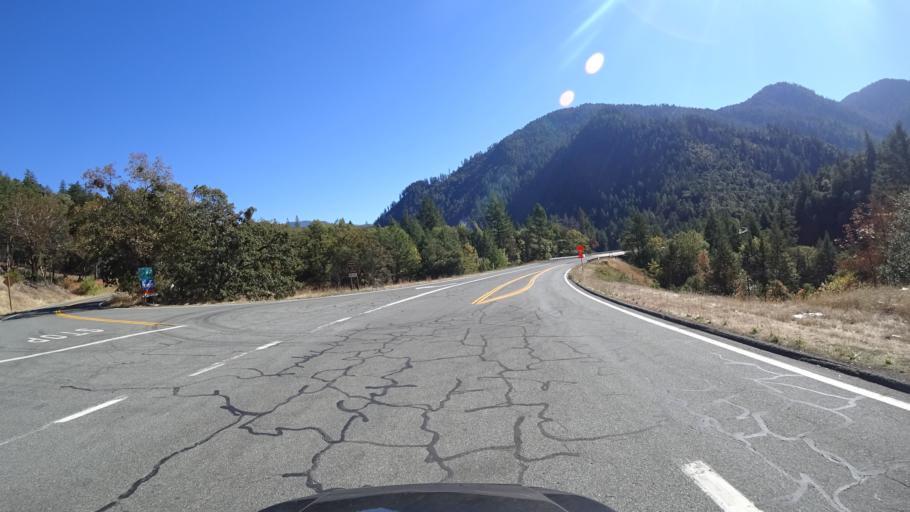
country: US
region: California
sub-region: Siskiyou County
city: Happy Camp
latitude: 41.3811
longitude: -123.4898
